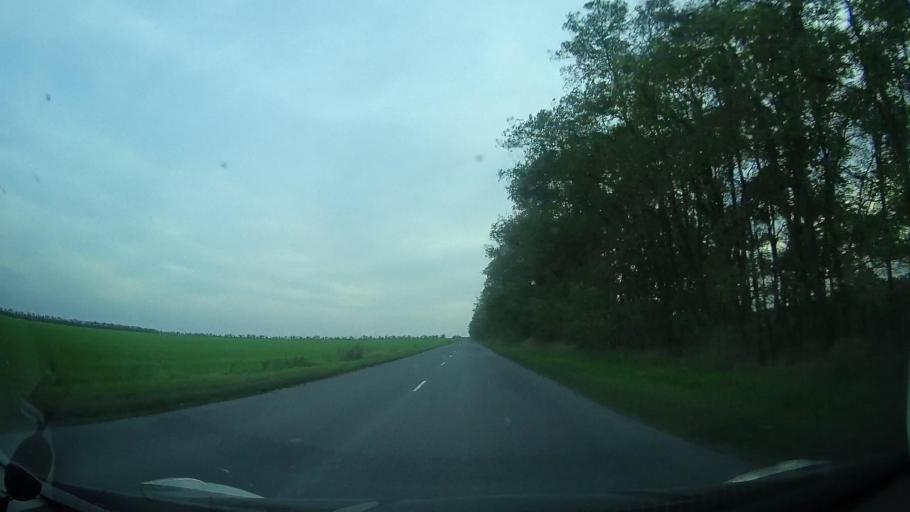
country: RU
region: Rostov
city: Kirovskaya
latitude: 47.0490
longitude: 39.9768
